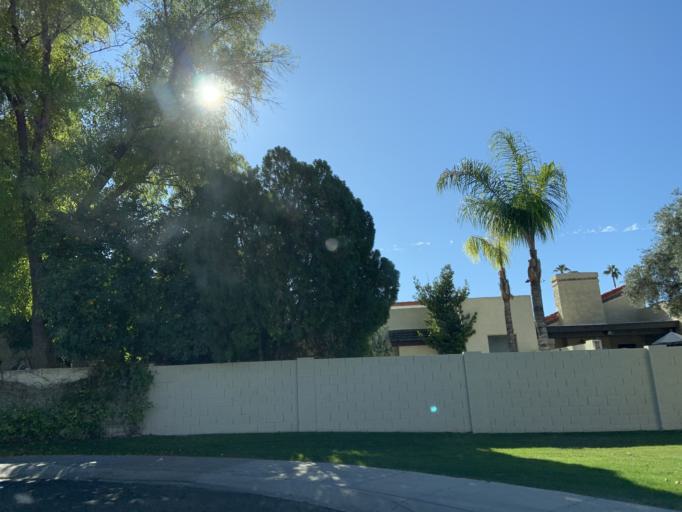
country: US
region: Arizona
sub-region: Maricopa County
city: San Carlos
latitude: 33.3658
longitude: -111.8785
